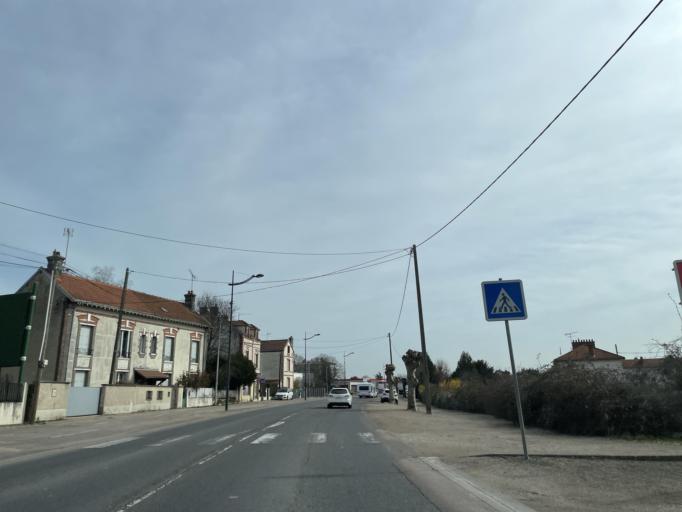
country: FR
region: Champagne-Ardenne
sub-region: Departement de l'Aube
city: Romilly-sur-Seine
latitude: 48.5115
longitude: 3.7171
